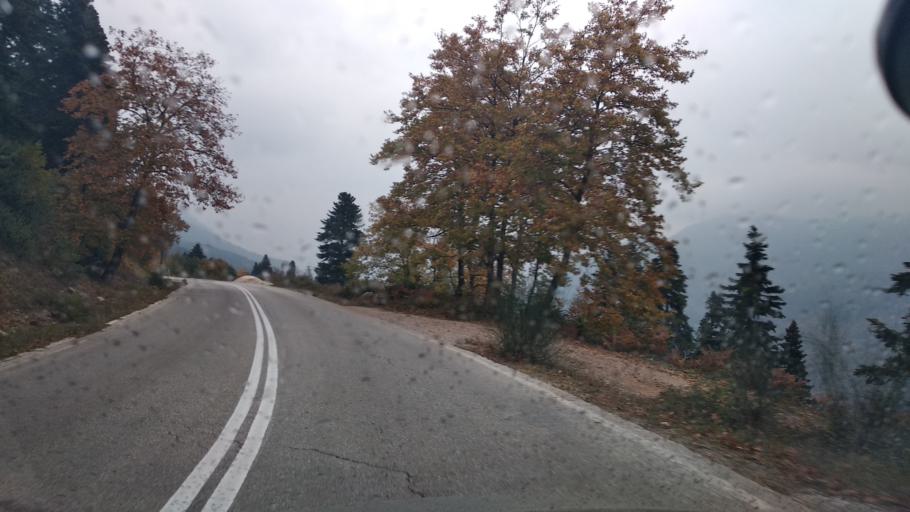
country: GR
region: Thessaly
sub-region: Trikala
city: Pyli
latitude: 39.5156
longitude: 21.5263
